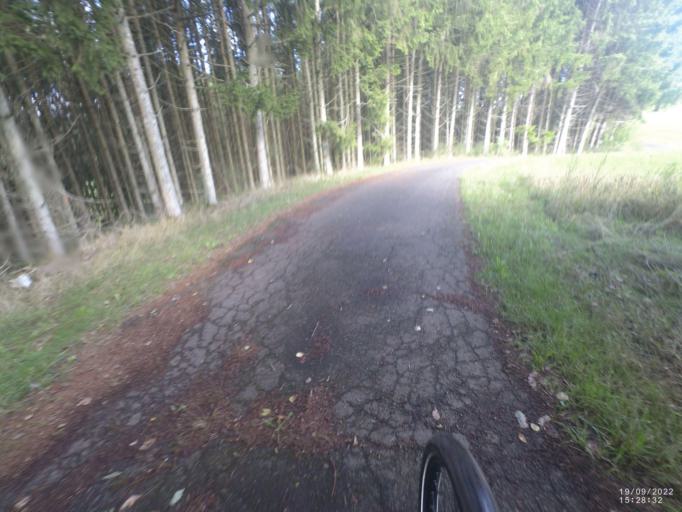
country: DE
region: Rheinland-Pfalz
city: Bleckhausen
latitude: 50.1498
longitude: 6.7816
